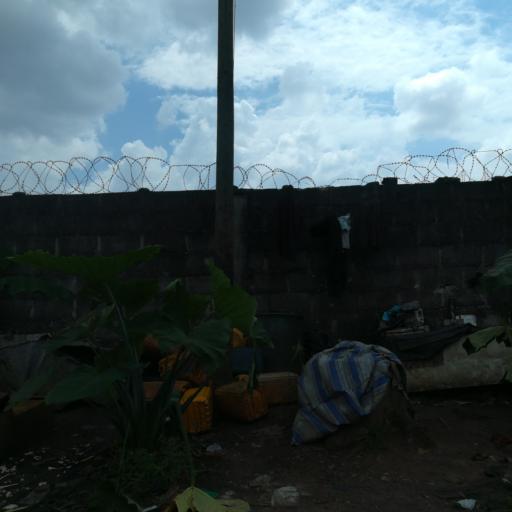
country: NG
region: Rivers
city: Port Harcourt
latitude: 4.8092
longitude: 7.0385
